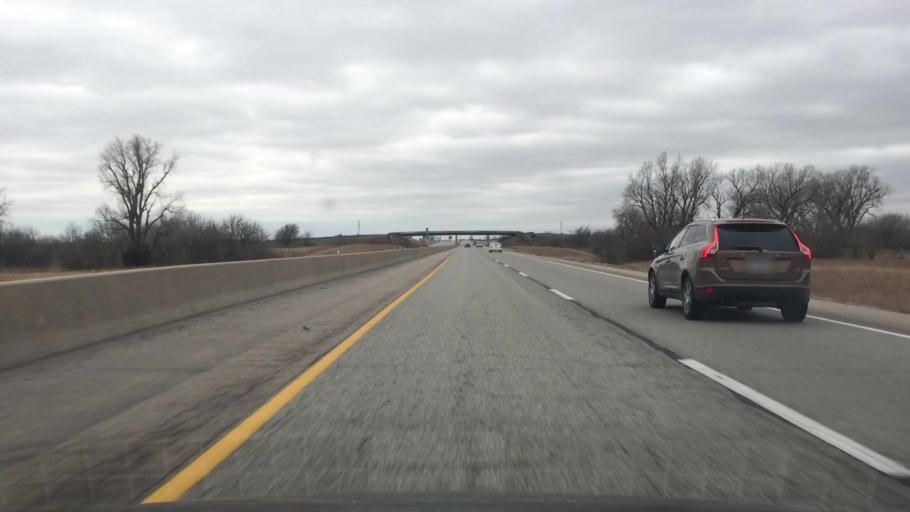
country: US
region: Kansas
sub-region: Butler County
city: El Dorado
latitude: 38.0313
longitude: -96.6571
